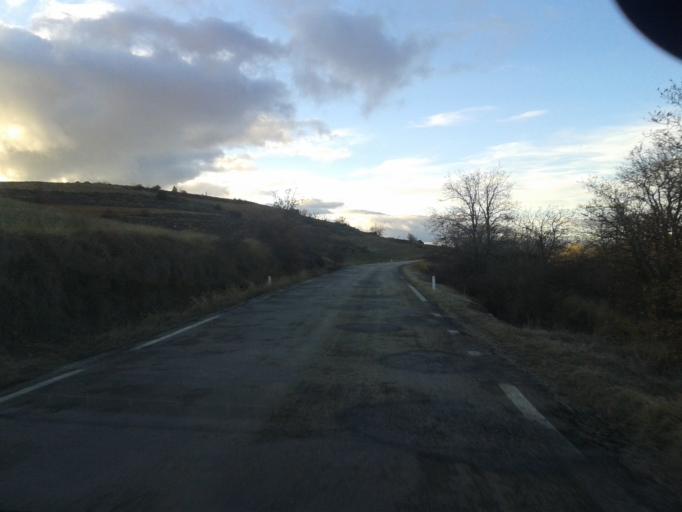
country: ES
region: Aragon
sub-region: Provincia de Teruel
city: Lagueruela
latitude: 41.0407
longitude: -1.2034
